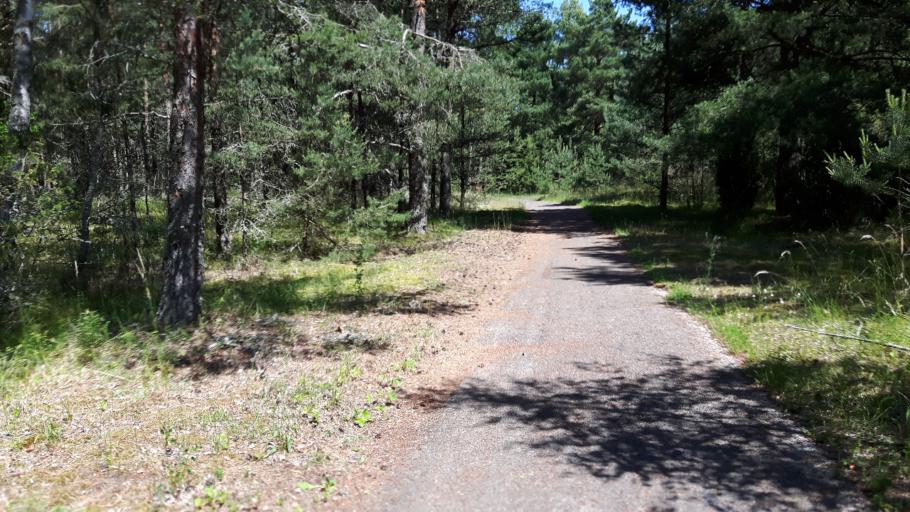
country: LT
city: Neringa
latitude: 55.4742
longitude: 21.0866
